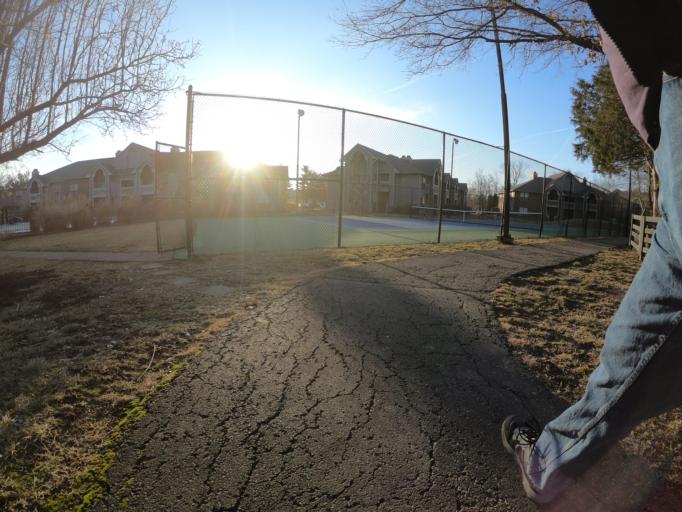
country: US
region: Kentucky
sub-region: Jefferson County
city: Lyndon
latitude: 38.2510
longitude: -85.6035
